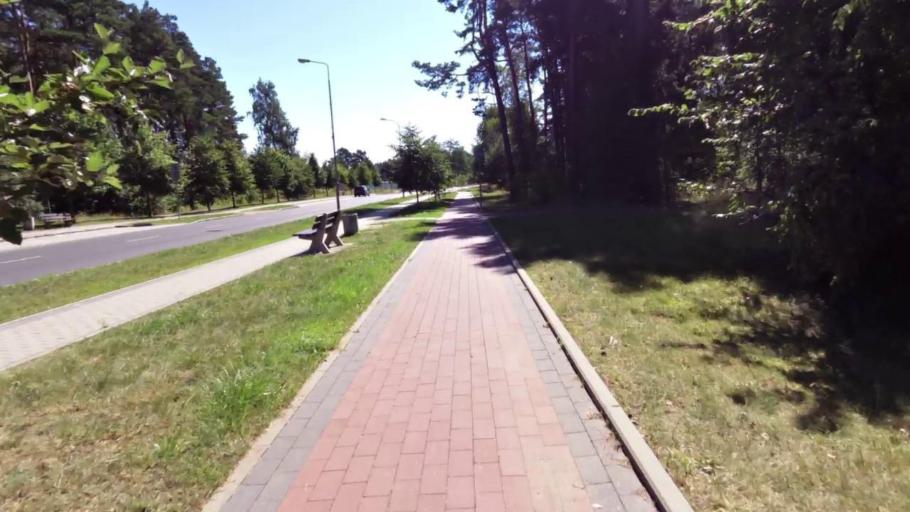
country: PL
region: West Pomeranian Voivodeship
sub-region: Powiat szczecinecki
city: Borne Sulinowo
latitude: 53.5804
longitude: 16.5477
